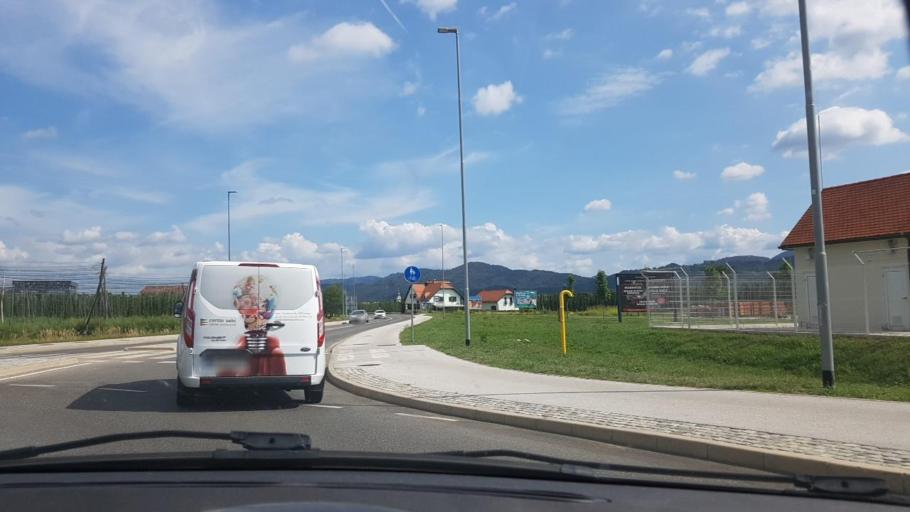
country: SI
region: Zalec
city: Zalec
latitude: 46.2512
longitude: 15.1779
